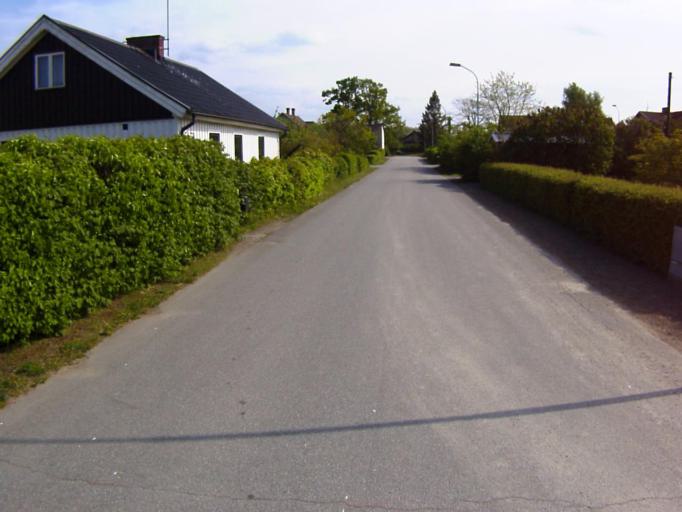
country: SE
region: Skane
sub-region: Kristianstads Kommun
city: Kristianstad
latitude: 56.0539
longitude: 14.0878
